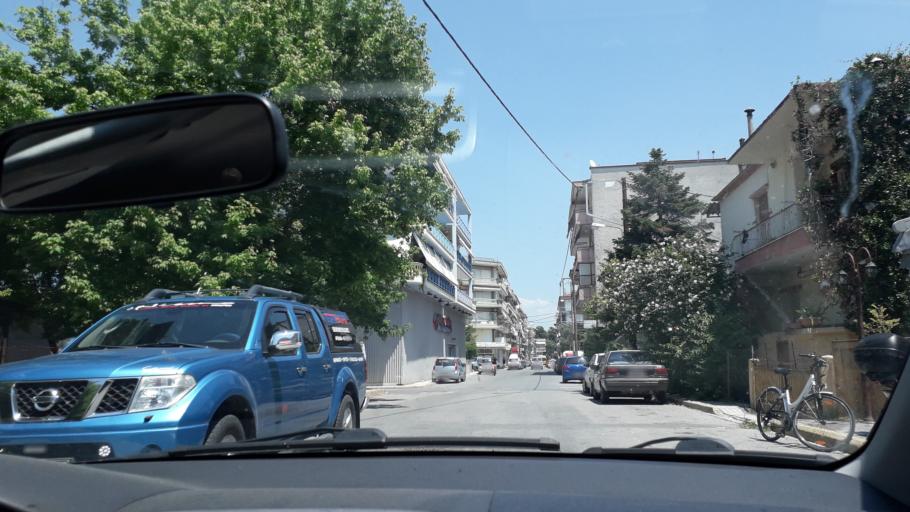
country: GR
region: Central Macedonia
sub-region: Nomos Pellis
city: Aridaia
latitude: 40.9724
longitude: 22.0598
